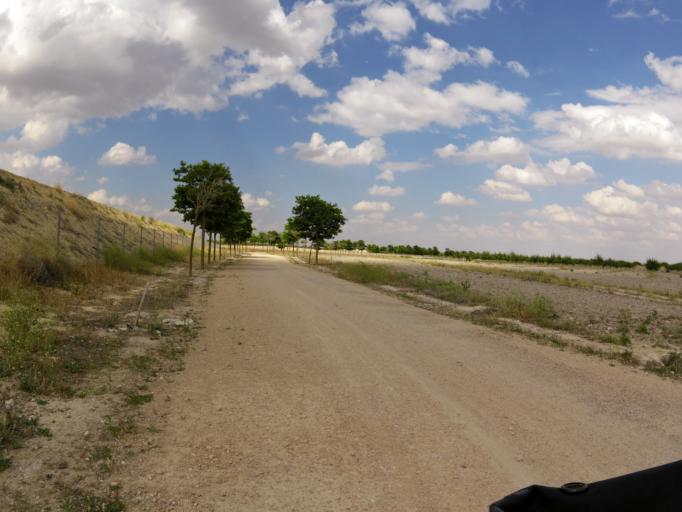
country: ES
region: Castille-La Mancha
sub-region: Provincia de Albacete
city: Albacete
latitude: 38.9569
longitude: -1.9771
